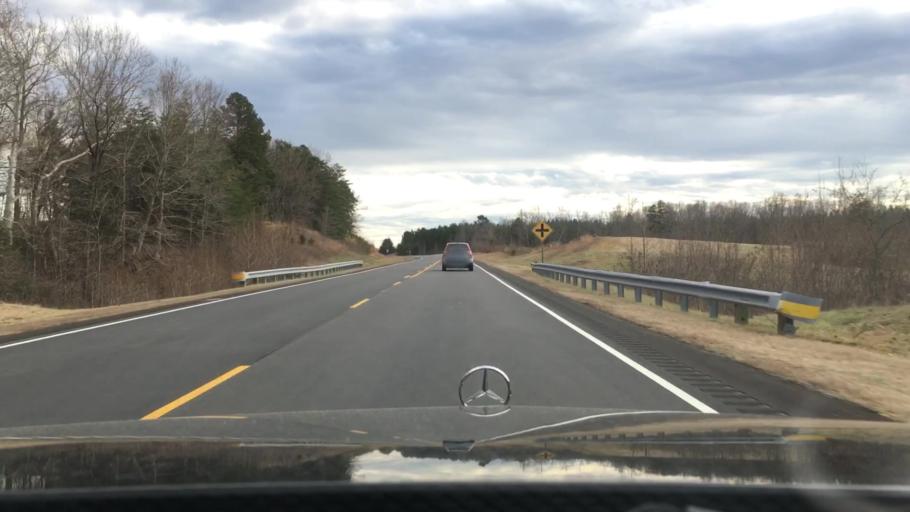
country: US
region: North Carolina
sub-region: Caswell County
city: Yanceyville
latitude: 36.3052
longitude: -79.2177
